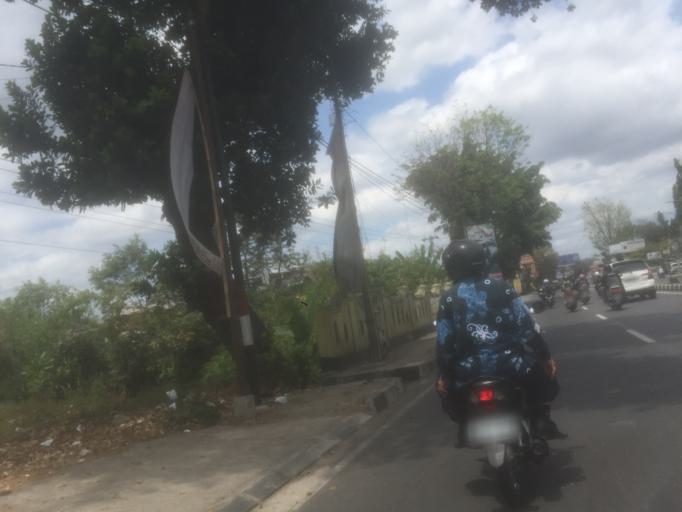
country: ID
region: Daerah Istimewa Yogyakarta
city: Melati
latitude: -7.7242
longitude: 110.3621
